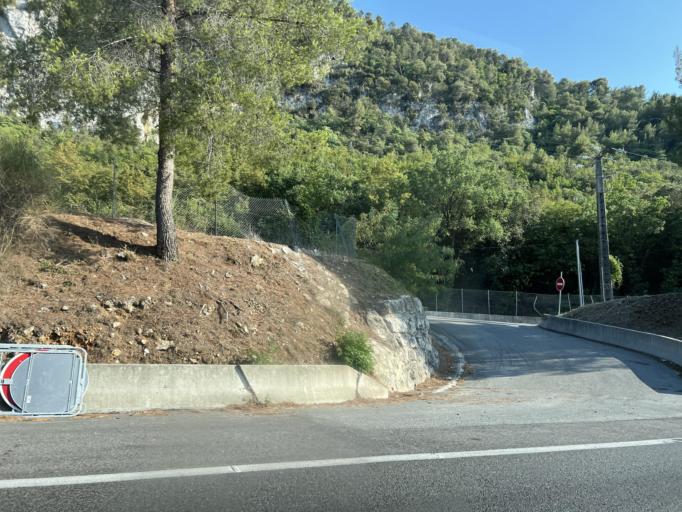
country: FR
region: Provence-Alpes-Cote d'Azur
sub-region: Departement des Alpes-Maritimes
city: Drap
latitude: 43.7432
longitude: 7.3448
